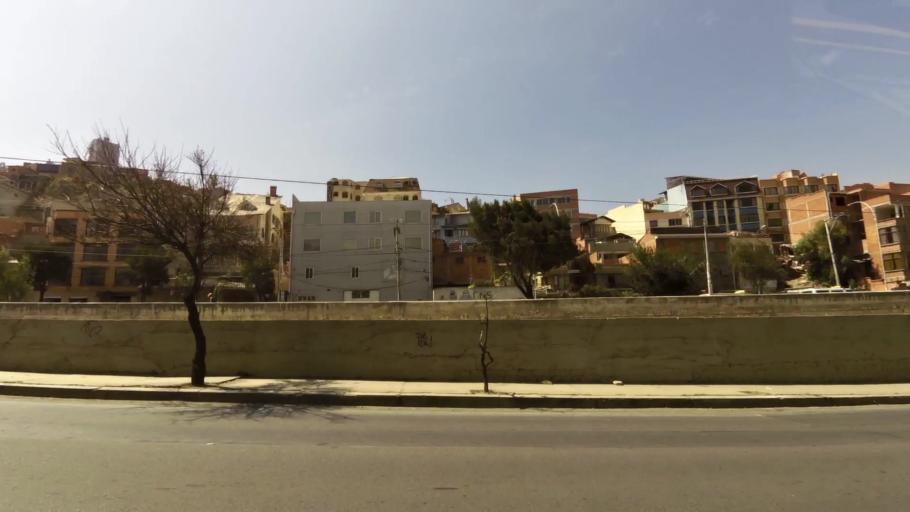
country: BO
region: La Paz
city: La Paz
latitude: -16.5406
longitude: -68.0945
